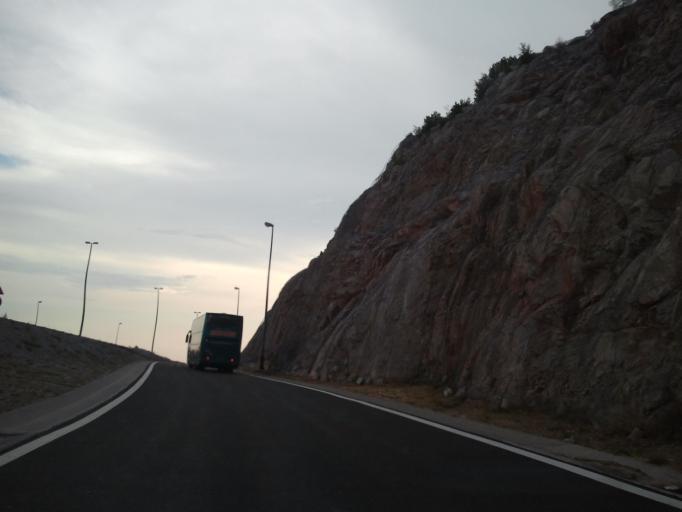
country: HR
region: Zadarska
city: Obrovac
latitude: 44.2518
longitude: 15.6394
